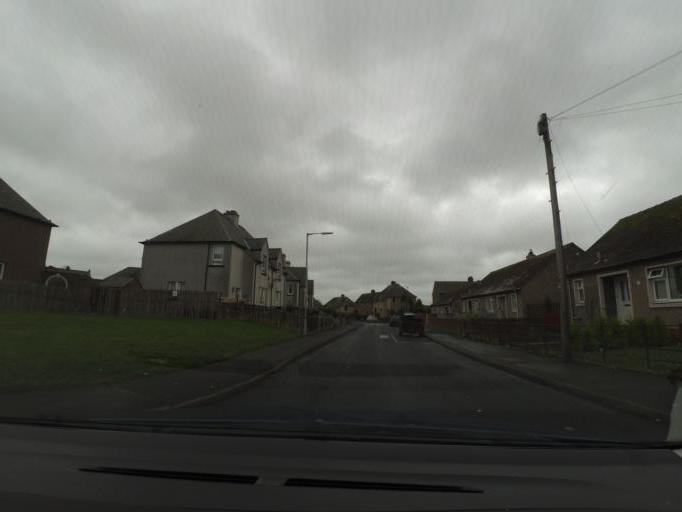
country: GB
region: Scotland
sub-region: The Scottish Borders
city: Hawick
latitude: 55.4351
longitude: -2.7725
